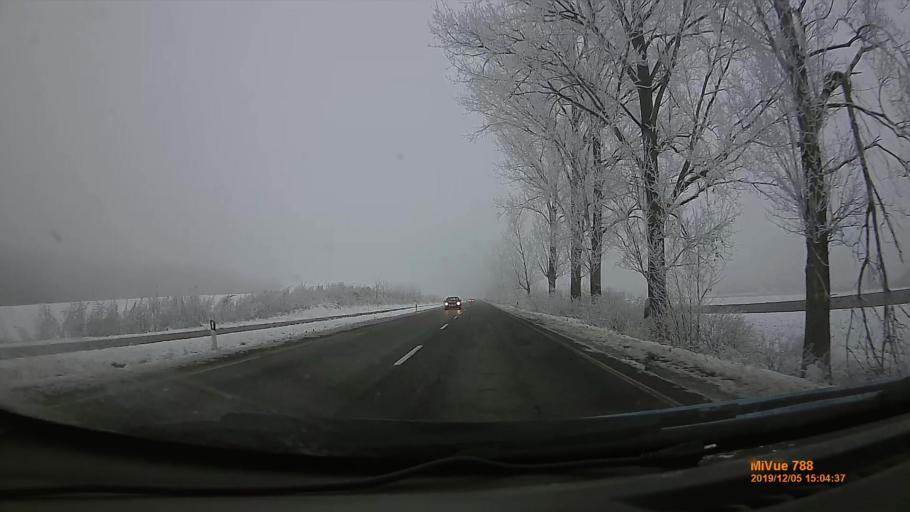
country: HU
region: Szabolcs-Szatmar-Bereg
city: Tiszanagyfalu
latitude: 48.0992
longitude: 21.4919
